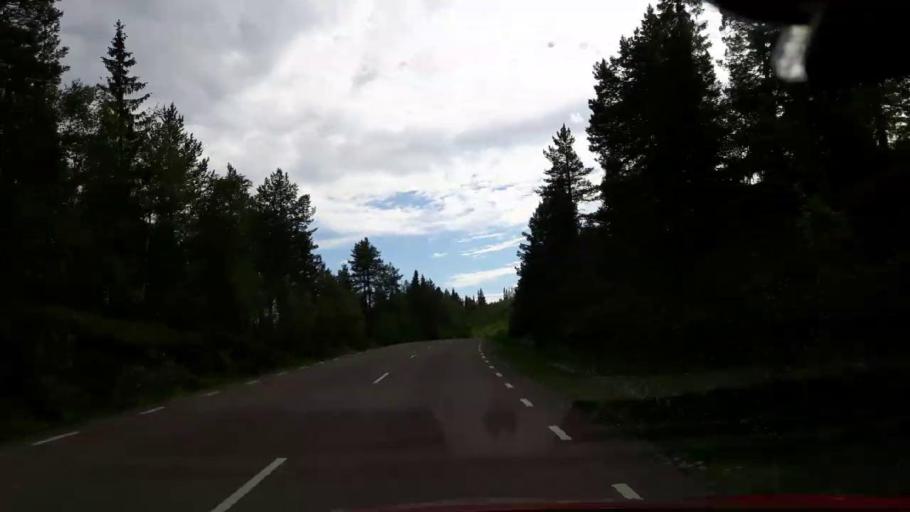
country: SE
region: Jaemtland
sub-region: Krokoms Kommun
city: Valla
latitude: 63.9422
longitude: 14.2246
